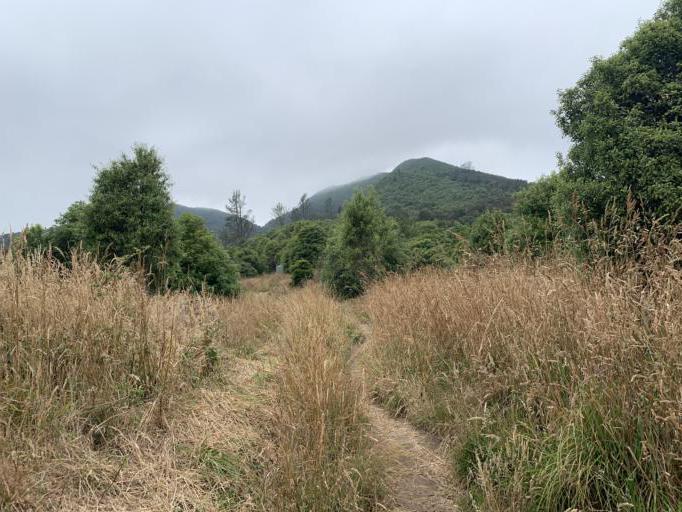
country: NZ
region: Waikato
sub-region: Taupo District
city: Taupo
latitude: -38.6985
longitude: 176.1449
